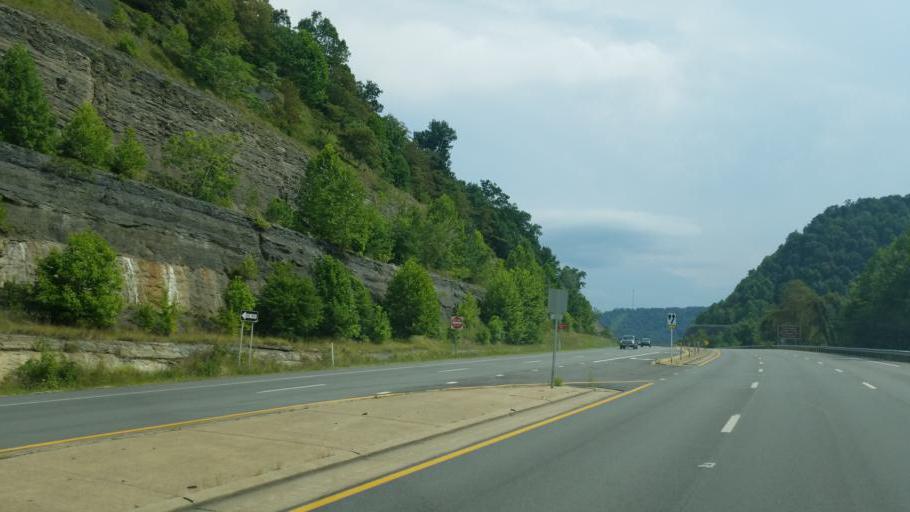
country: US
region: West Virginia
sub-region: Logan County
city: Chapmanville
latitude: 37.9149
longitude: -82.0373
